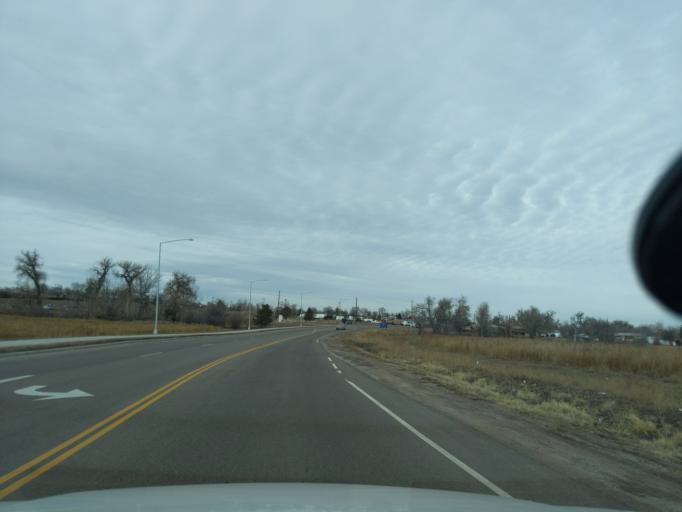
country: US
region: Colorado
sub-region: Adams County
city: Welby
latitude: 39.8572
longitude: -104.9497
